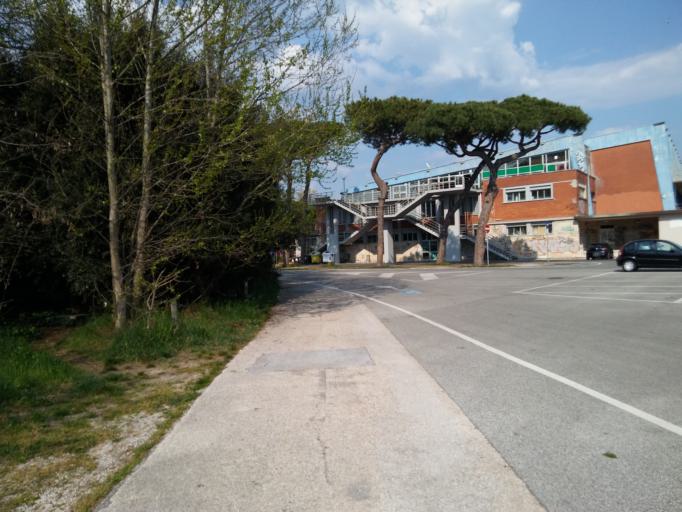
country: IT
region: Tuscany
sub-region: Provincia di Lucca
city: Viareggio
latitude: 43.8580
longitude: 10.2475
